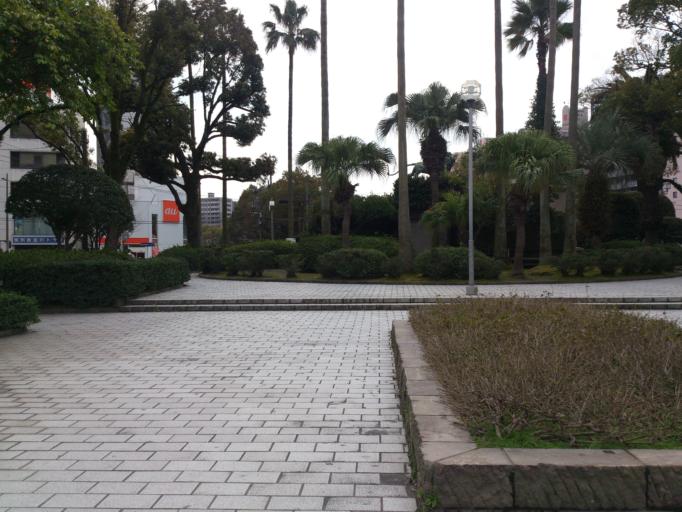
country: JP
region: Kagoshima
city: Kagoshima-shi
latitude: 31.5870
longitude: 130.5461
